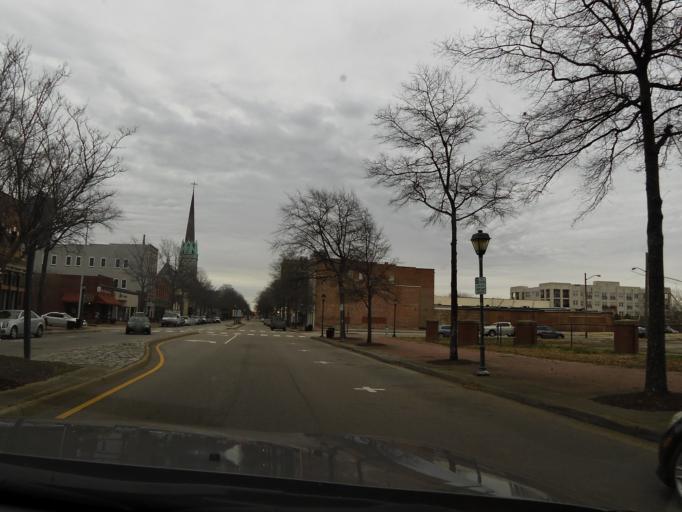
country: US
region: Virginia
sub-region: City of Portsmouth
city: Portsmouth
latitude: 36.8352
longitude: -76.3061
